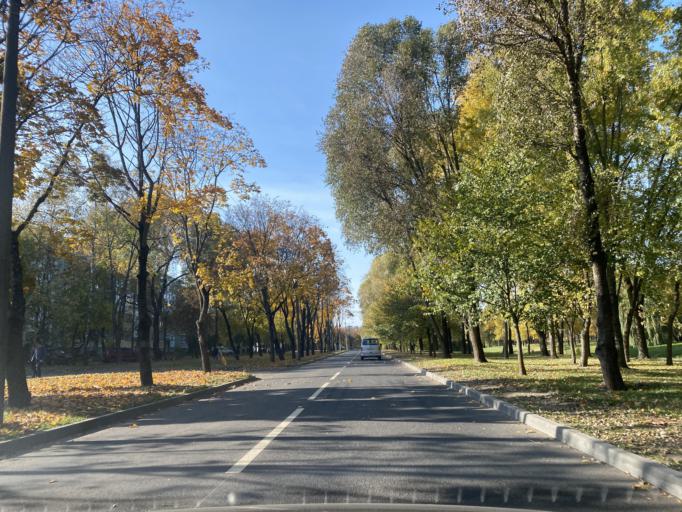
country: BY
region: Minsk
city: Borovlyany
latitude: 53.9486
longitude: 27.6364
